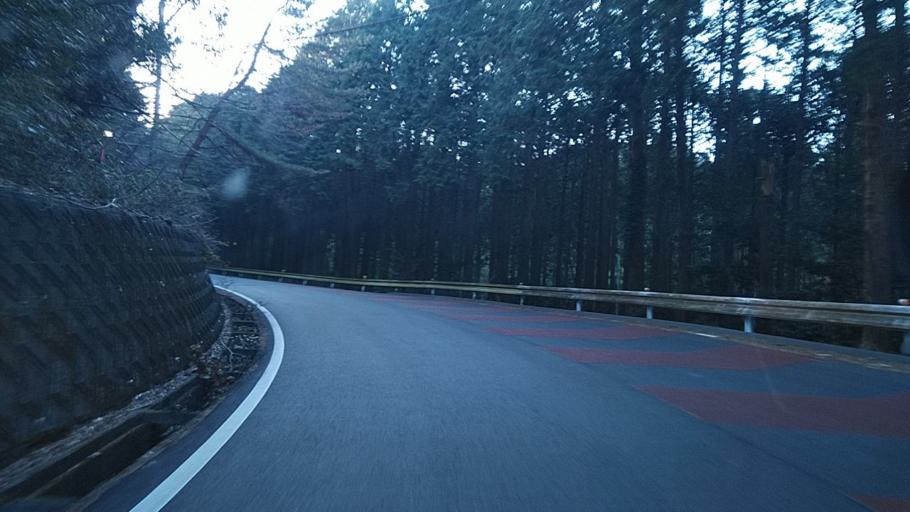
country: JP
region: Chiba
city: Kimitsu
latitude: 35.2577
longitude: 139.9504
